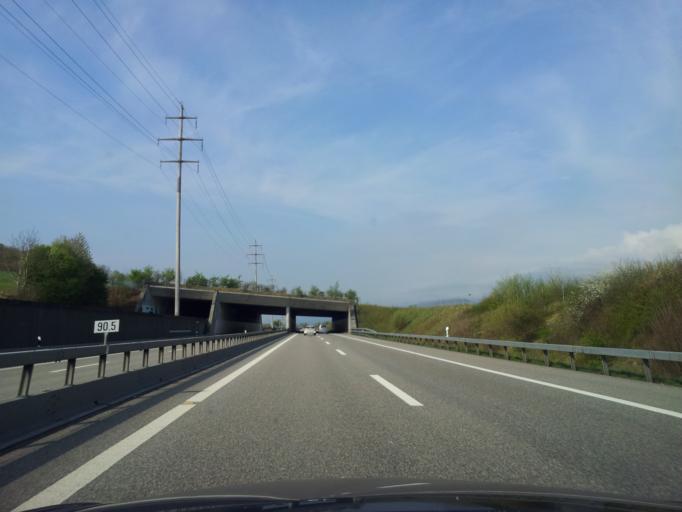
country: CH
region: Bern
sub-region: Seeland District
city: Leuzigen
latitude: 47.1908
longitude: 7.4871
